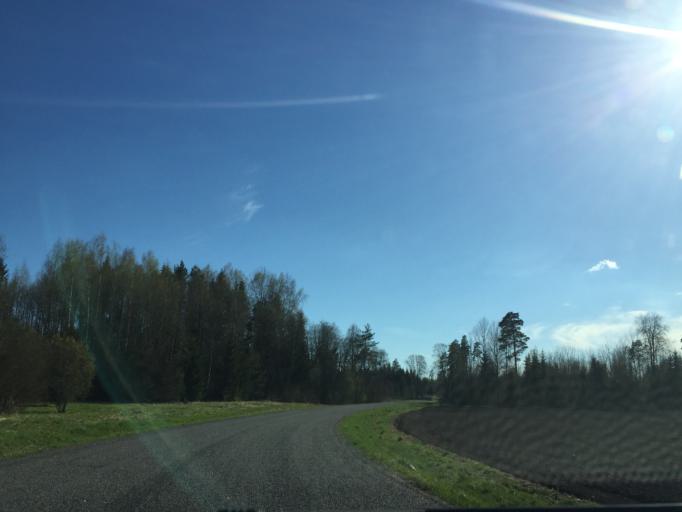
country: EE
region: Valgamaa
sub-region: Valga linn
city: Valga
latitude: 57.8500
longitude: 26.2525
